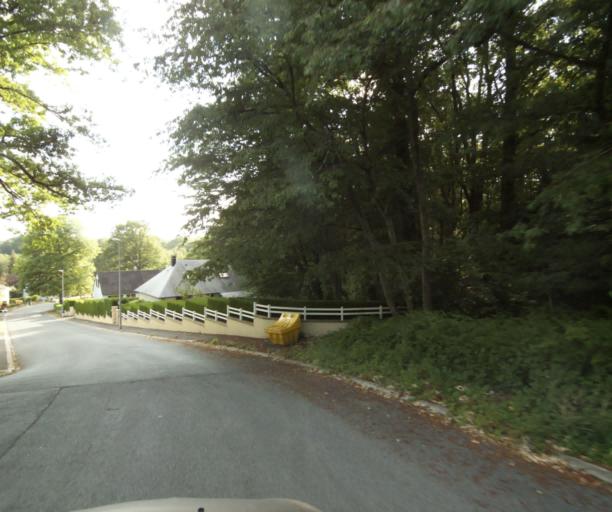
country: FR
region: Champagne-Ardenne
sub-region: Departement des Ardennes
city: Charleville-Mezieres
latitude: 49.7968
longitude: 4.7095
